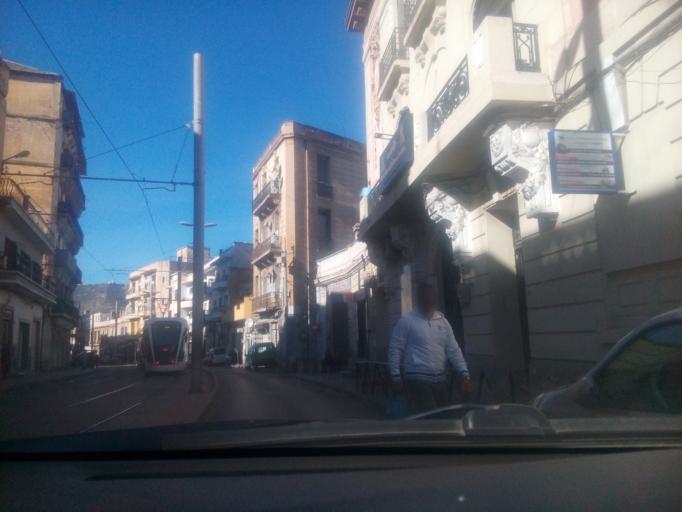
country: DZ
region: Oran
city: Oran
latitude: 35.6995
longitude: -0.6370
